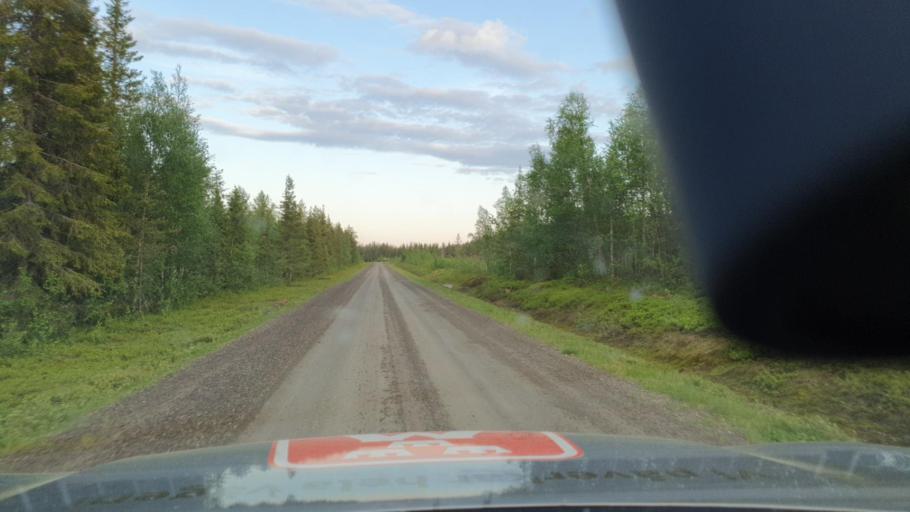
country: SE
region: Norrbotten
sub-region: Bodens Kommun
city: Boden
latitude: 66.5256
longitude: 21.4925
